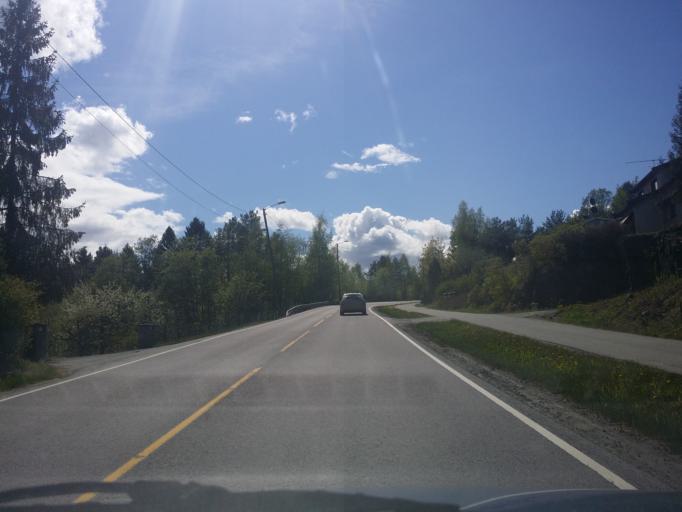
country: NO
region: Buskerud
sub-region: Ringerike
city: Honefoss
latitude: 60.0978
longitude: 10.1151
